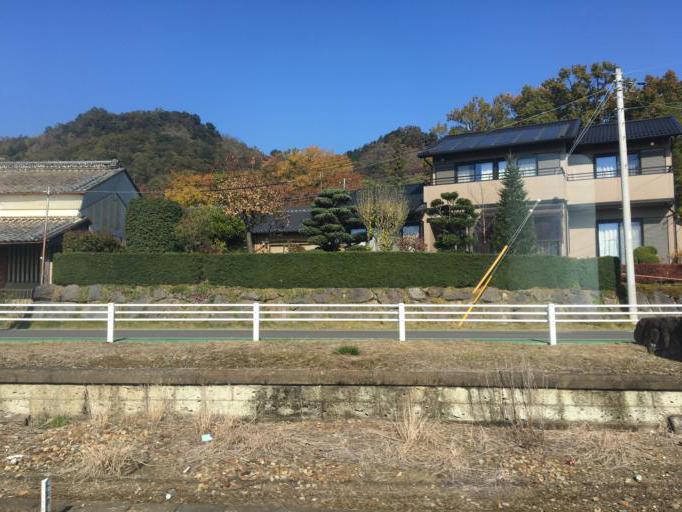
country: JP
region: Tochigi
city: Sano
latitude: 36.3267
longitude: 139.6592
